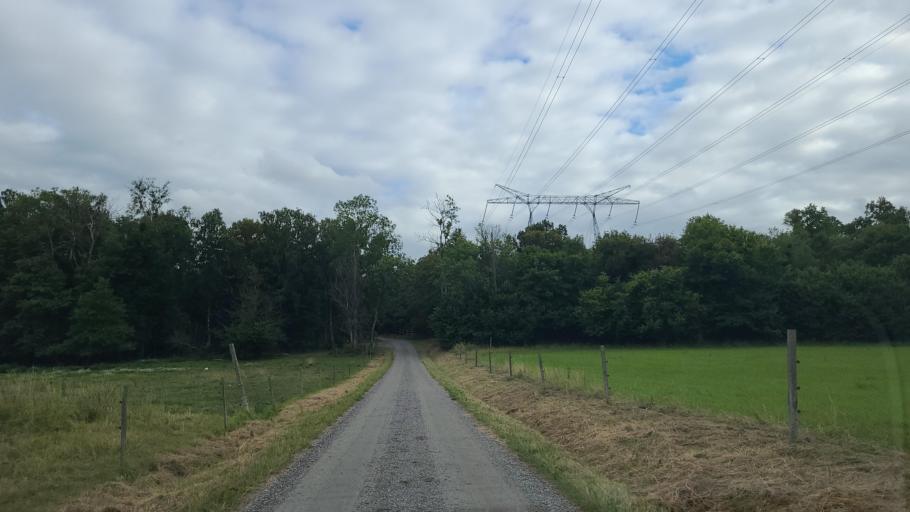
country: SE
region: Stockholm
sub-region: Upplands-Bro Kommun
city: Bro
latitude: 59.4580
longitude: 17.5812
